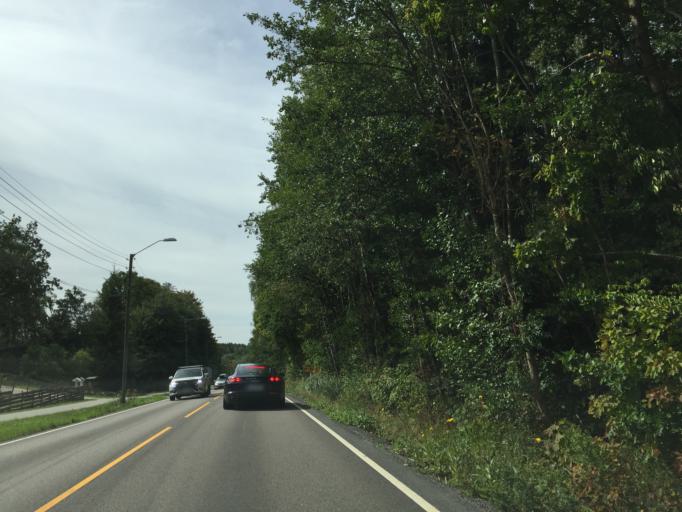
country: NO
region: Ostfold
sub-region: Fredrikstad
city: Fredrikstad
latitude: 59.1847
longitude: 10.9281
